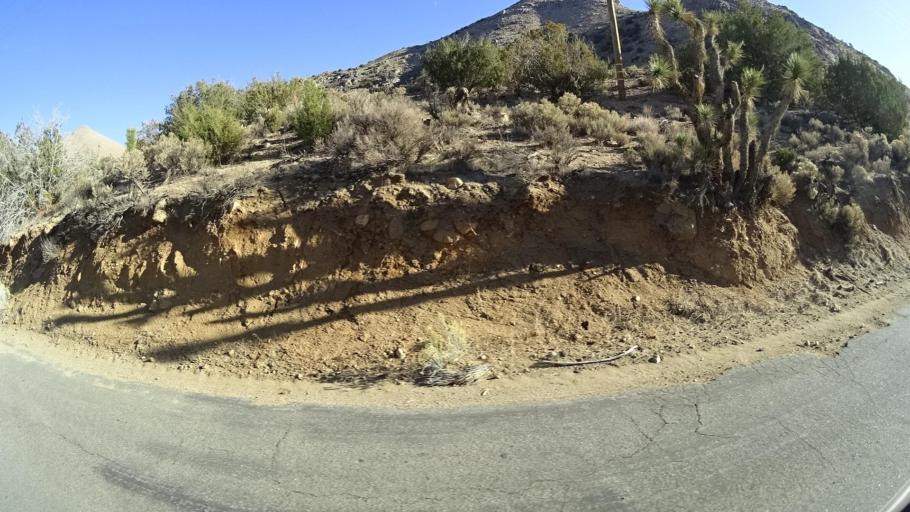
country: US
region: California
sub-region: Kern County
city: Weldon
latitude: 35.5830
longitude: -118.2481
